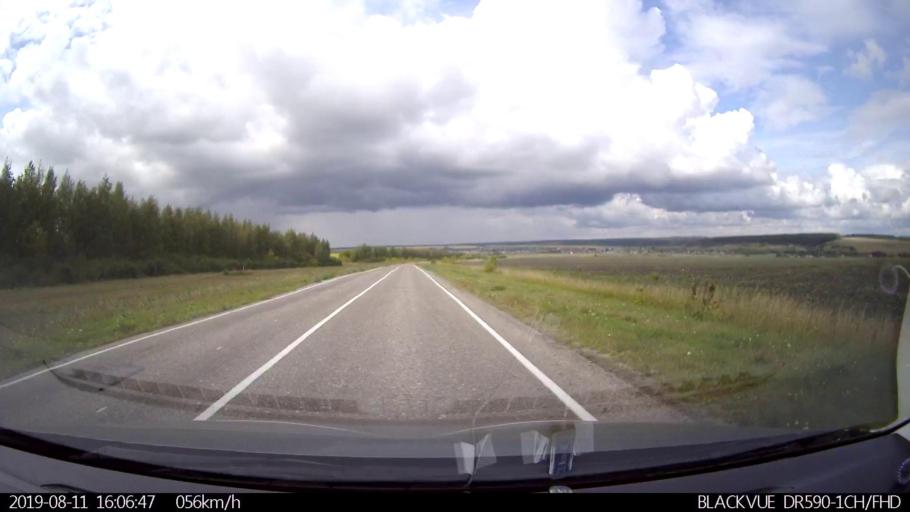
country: RU
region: Ulyanovsk
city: Ignatovka
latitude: 53.9717
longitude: 47.6475
